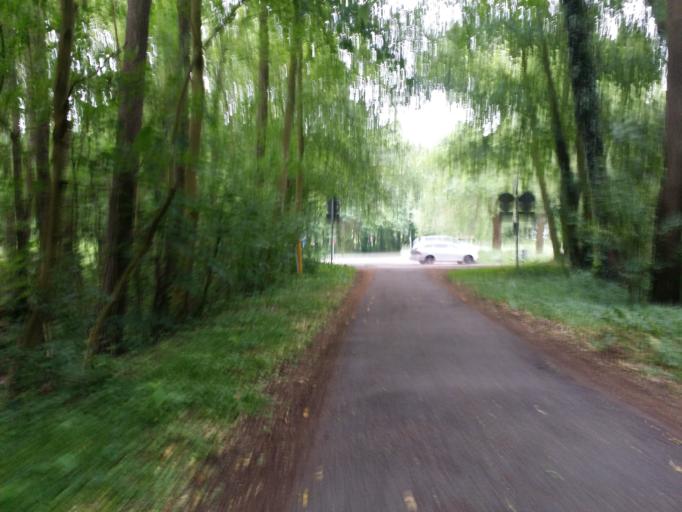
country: DE
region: Lower Saxony
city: Oldenburg
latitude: 53.1499
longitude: 8.2795
